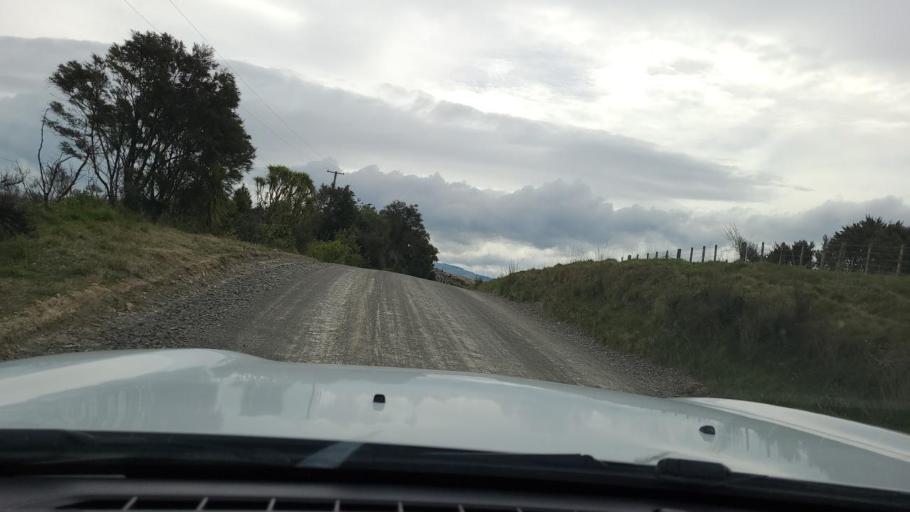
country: NZ
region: Hawke's Bay
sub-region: Napier City
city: Napier
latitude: -39.3376
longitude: 176.8305
